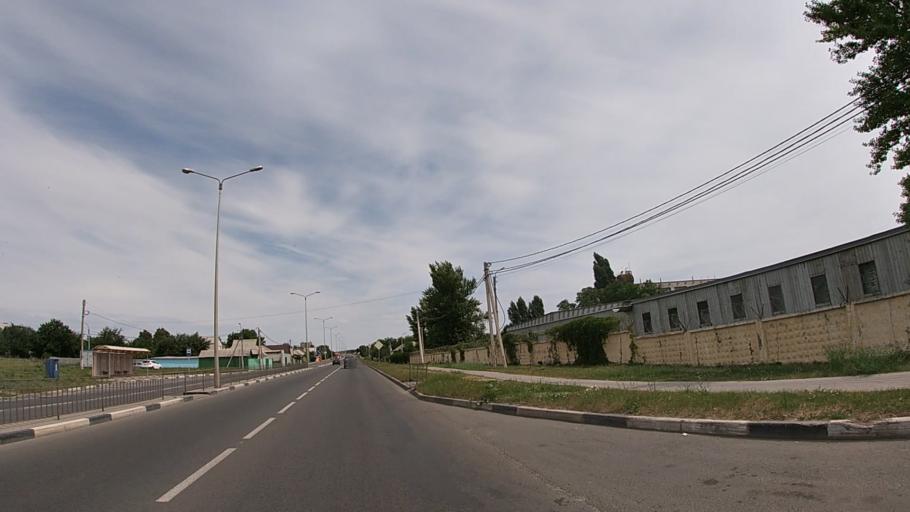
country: RU
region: Belgorod
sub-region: Belgorodskiy Rayon
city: Belgorod
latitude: 50.6192
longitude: 36.5400
